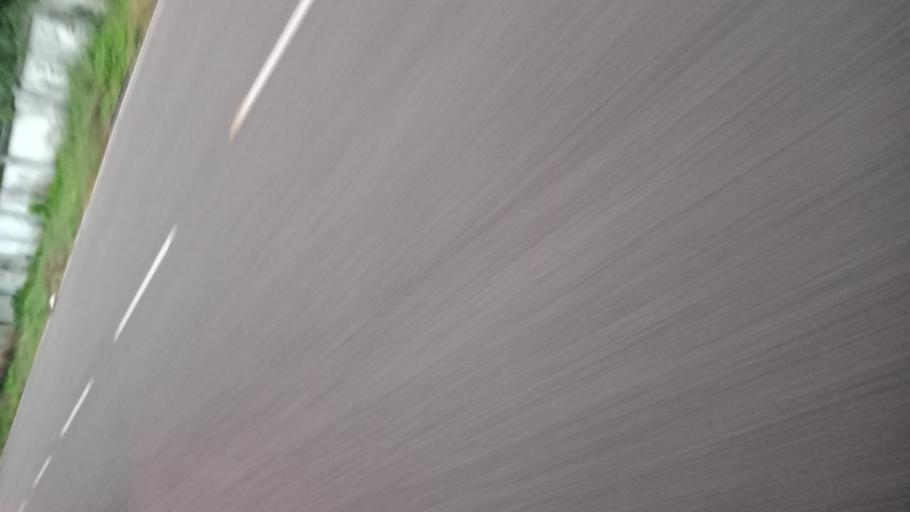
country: IN
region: Telangana
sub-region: Medak
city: Serilingampalle
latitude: 17.4960
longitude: 78.3086
